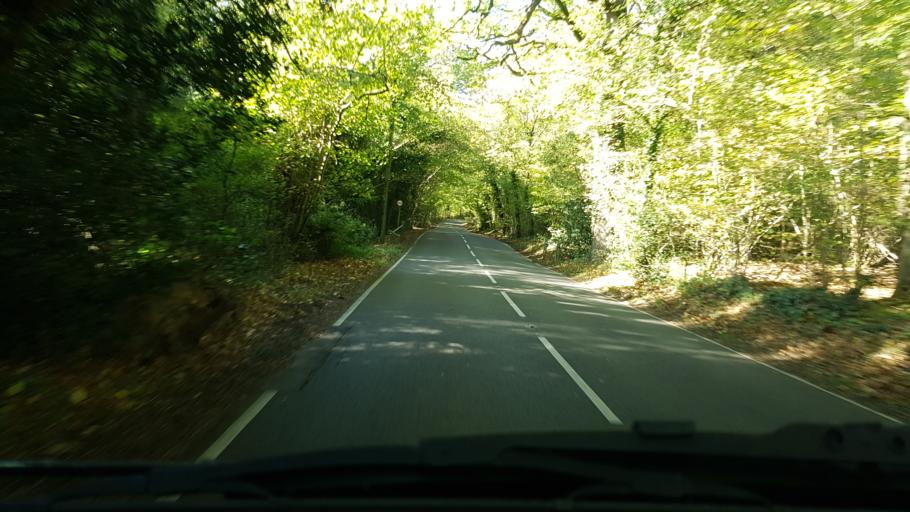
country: GB
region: England
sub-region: Surrey
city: Ockley
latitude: 51.1611
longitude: -0.3838
